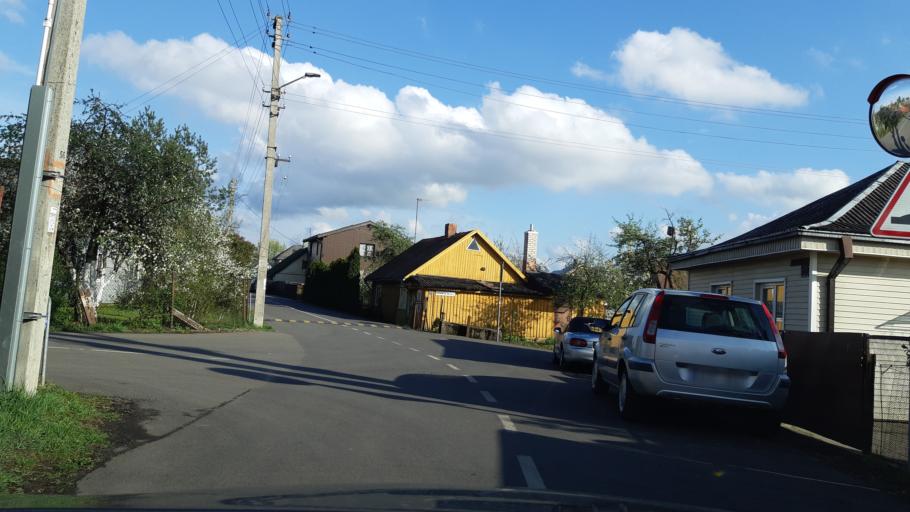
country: LT
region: Kauno apskritis
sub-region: Kaunas
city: Aleksotas
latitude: 54.8645
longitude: 23.9341
